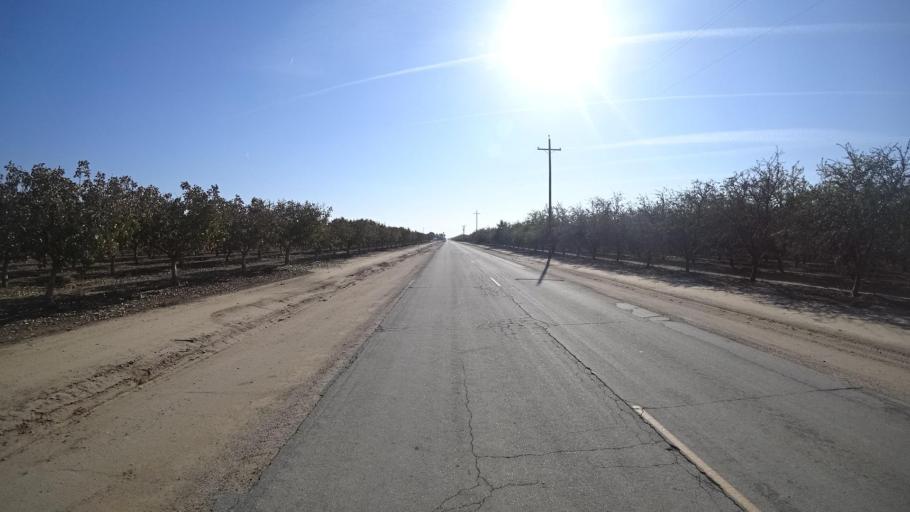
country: US
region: California
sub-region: Kern County
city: Wasco
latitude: 35.6581
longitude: -119.3486
